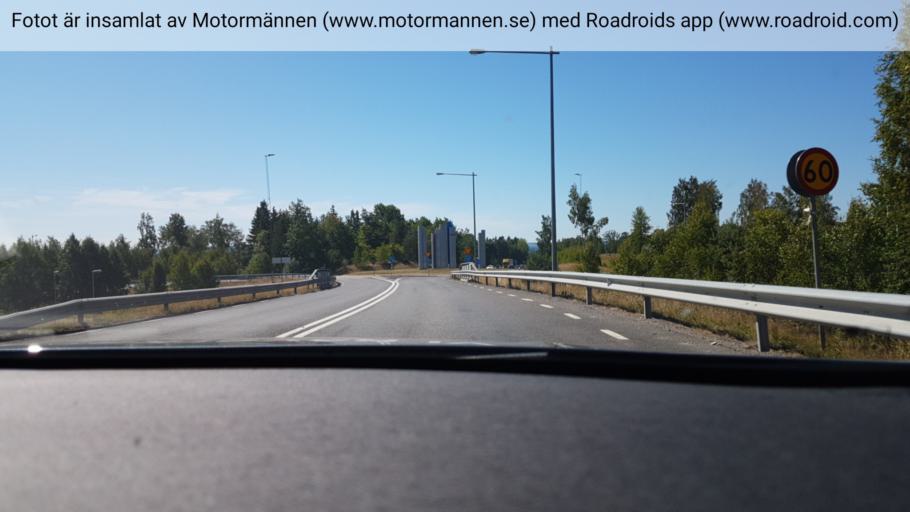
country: SE
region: Joenkoeping
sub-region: Habo Kommun
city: Habo
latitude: 57.9003
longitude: 14.1054
